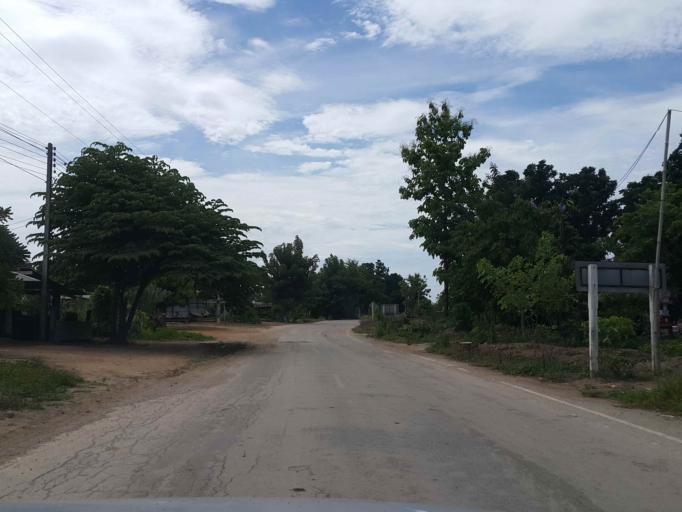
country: TH
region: Sukhothai
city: Ban Dan Lan Hoi
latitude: 17.0746
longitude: 99.4815
